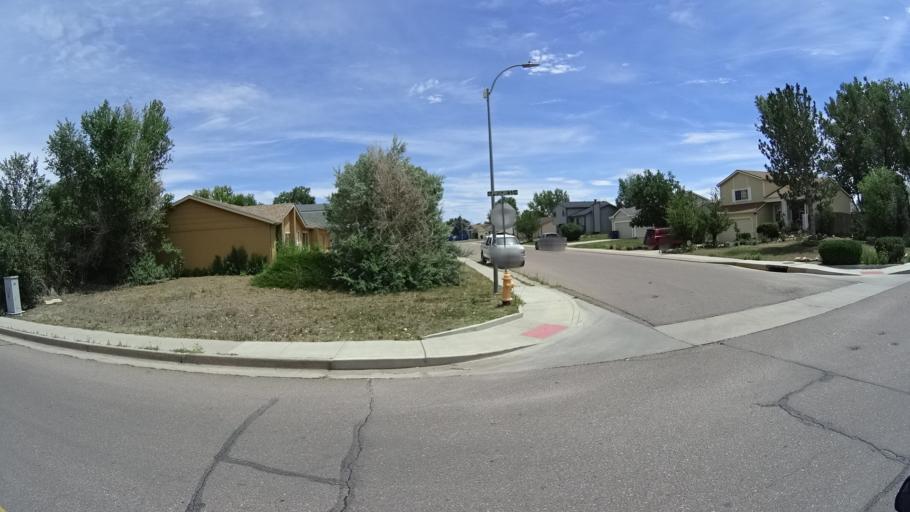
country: US
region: Colorado
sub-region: El Paso County
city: Fountain
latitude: 38.6668
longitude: -104.6766
